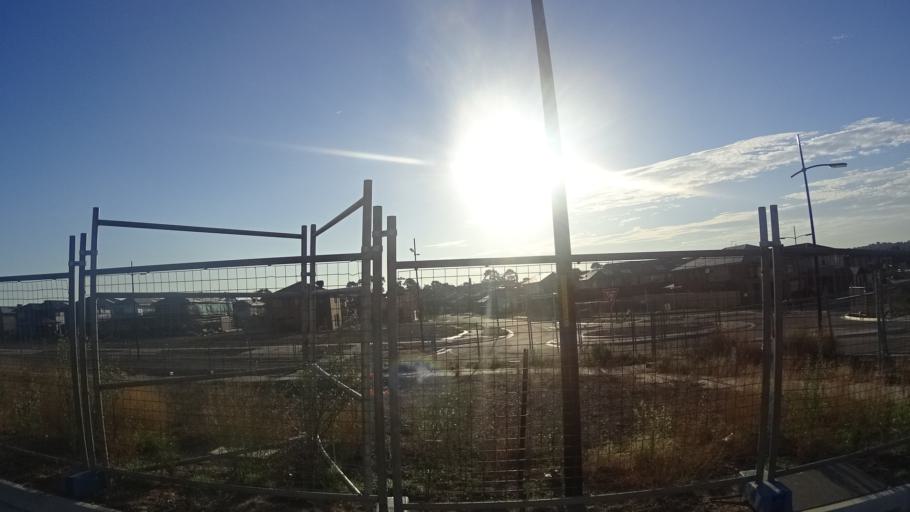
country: AU
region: Victoria
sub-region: Knox
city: Knoxfield
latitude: -37.8827
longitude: 145.2385
